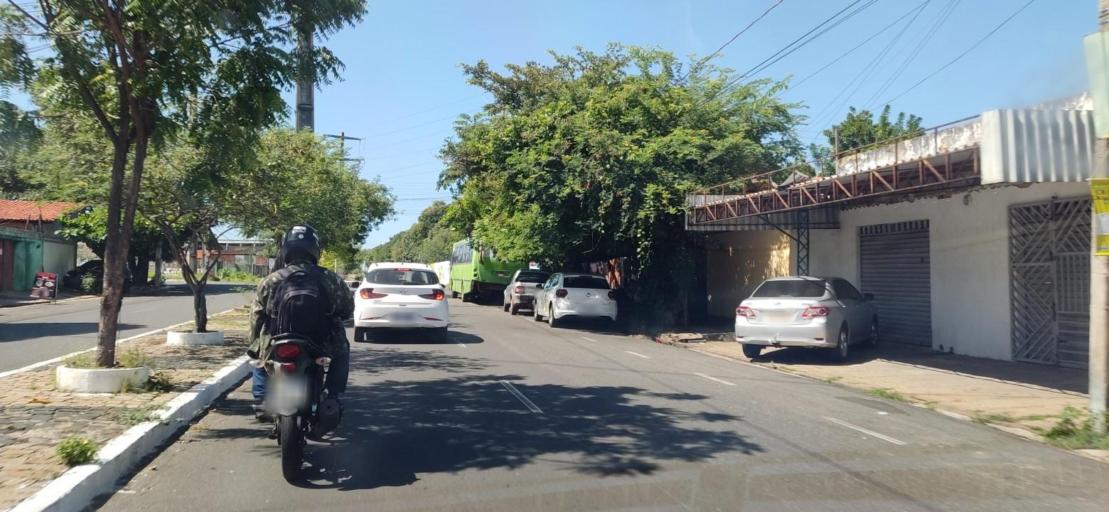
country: BR
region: Piaui
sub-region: Teresina
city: Teresina
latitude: -5.1218
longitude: -42.8088
